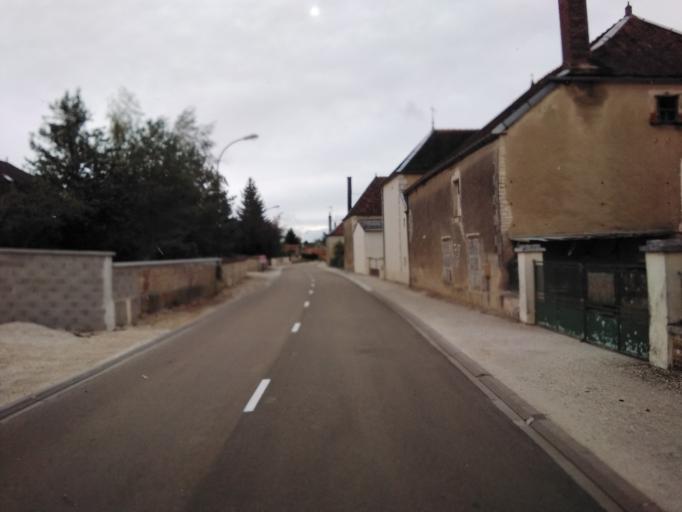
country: FR
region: Champagne-Ardenne
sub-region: Departement de l'Aube
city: Bar-sur-Seine
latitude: 48.1714
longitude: 4.4265
